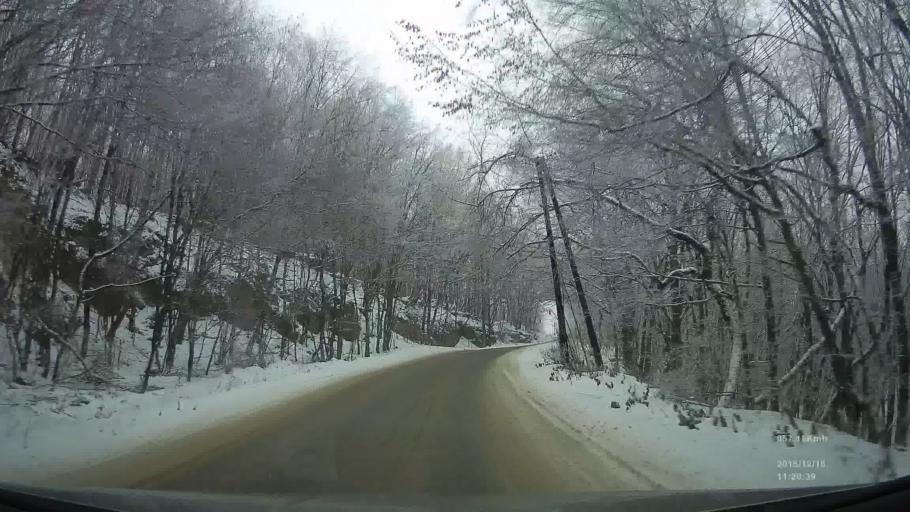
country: SK
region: Presovsky
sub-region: Okres Presov
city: Presov
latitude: 48.9088
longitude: 21.3619
